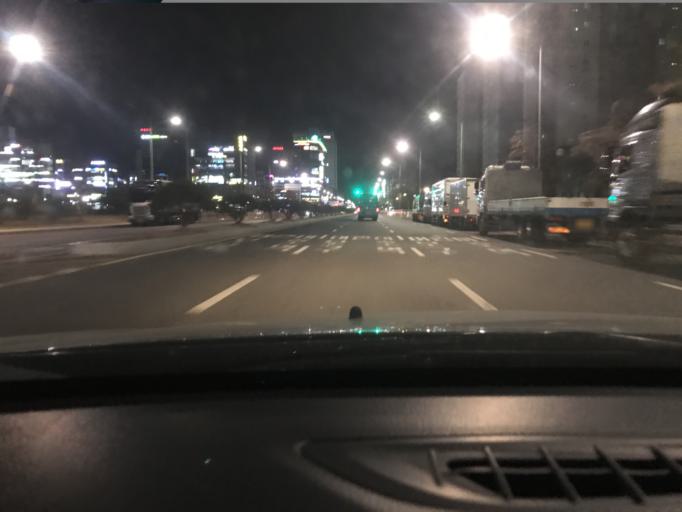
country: KR
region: Daegu
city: Hwawon
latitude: 35.6967
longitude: 128.4576
